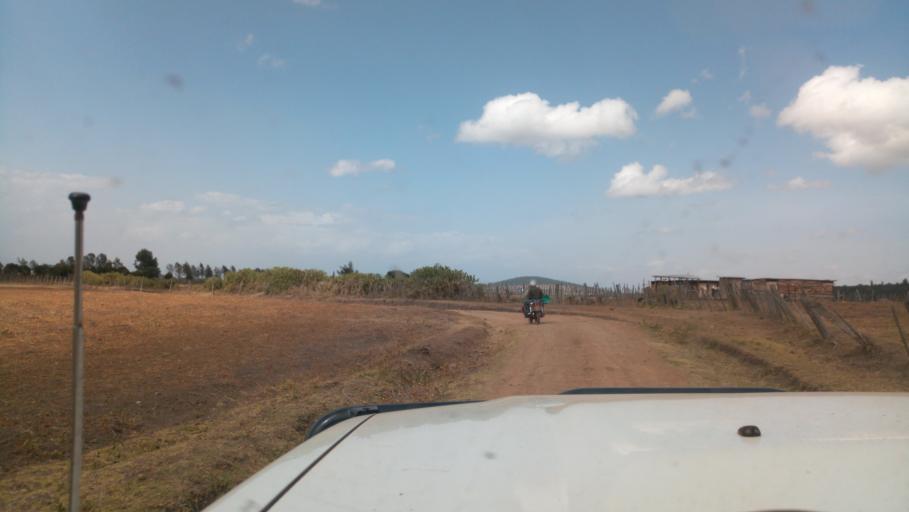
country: KE
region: Laikipia
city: Naro Moru
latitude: -0.1611
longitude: 36.7177
